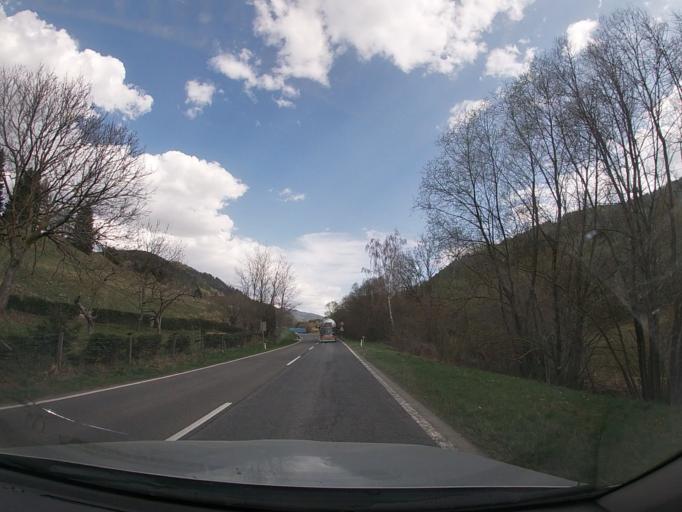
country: AT
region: Styria
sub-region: Politischer Bezirk Murau
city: Sankt Lorenzen bei Scheifling
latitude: 47.1410
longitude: 14.4224
